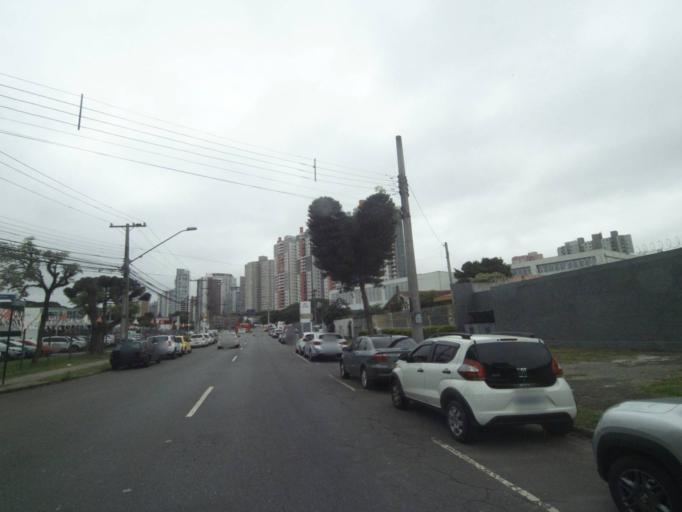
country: BR
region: Parana
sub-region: Curitiba
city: Curitiba
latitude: -25.4341
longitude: -49.3091
